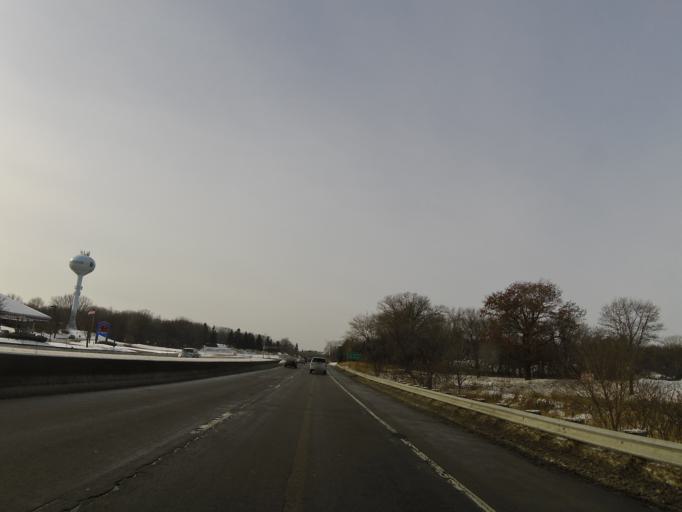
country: US
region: Minnesota
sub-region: Hennepin County
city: Deephaven
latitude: 44.9086
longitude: -93.5310
